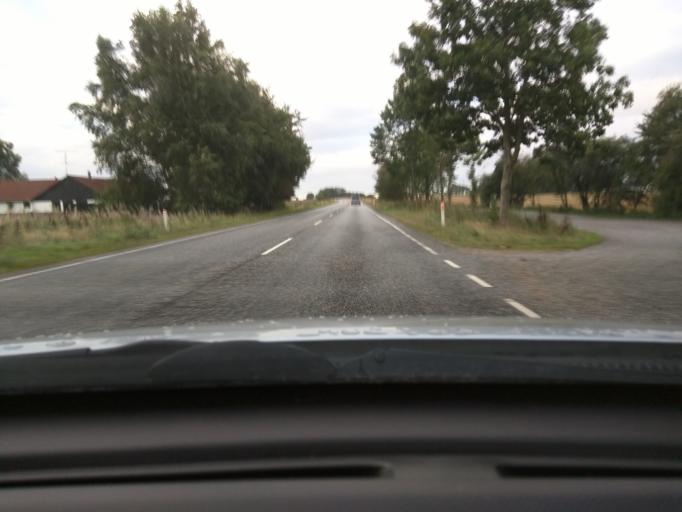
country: DK
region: Central Jutland
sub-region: Silkeborg Kommune
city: Kjellerup
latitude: 56.3131
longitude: 9.3280
